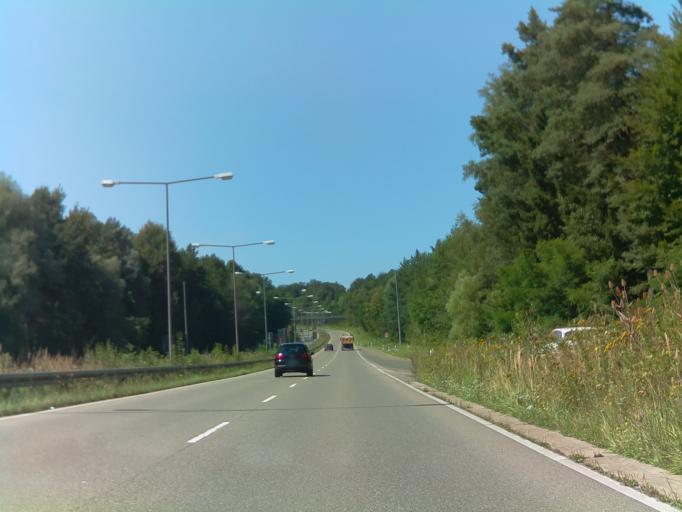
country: DE
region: Baden-Wuerttemberg
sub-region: Regierungsbezirk Stuttgart
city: Gerlingen
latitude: 48.7797
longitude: 9.0875
